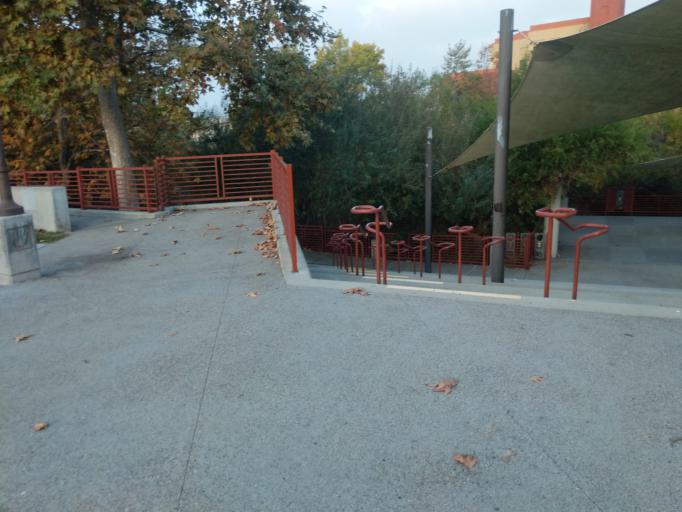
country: US
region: California
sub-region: San Diego County
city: National City
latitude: 32.7084
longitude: -117.0869
